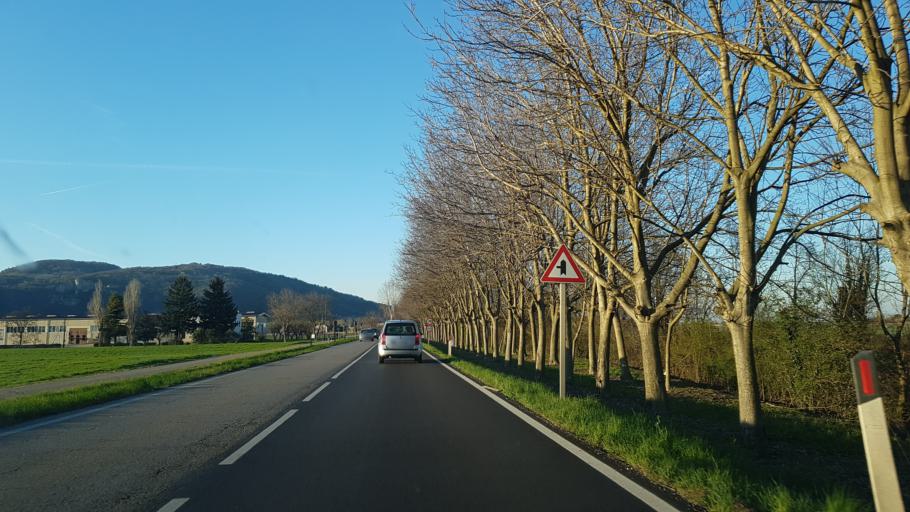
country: IT
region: Veneto
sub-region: Provincia di Vicenza
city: Ponte di Castegnero
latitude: 45.4471
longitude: 11.6011
